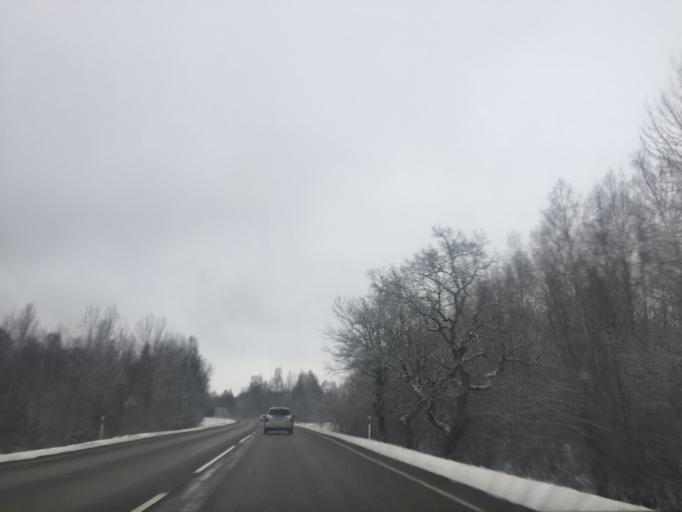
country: EE
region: Laeaene
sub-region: Lihula vald
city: Lihula
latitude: 58.6304
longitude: 23.6852
